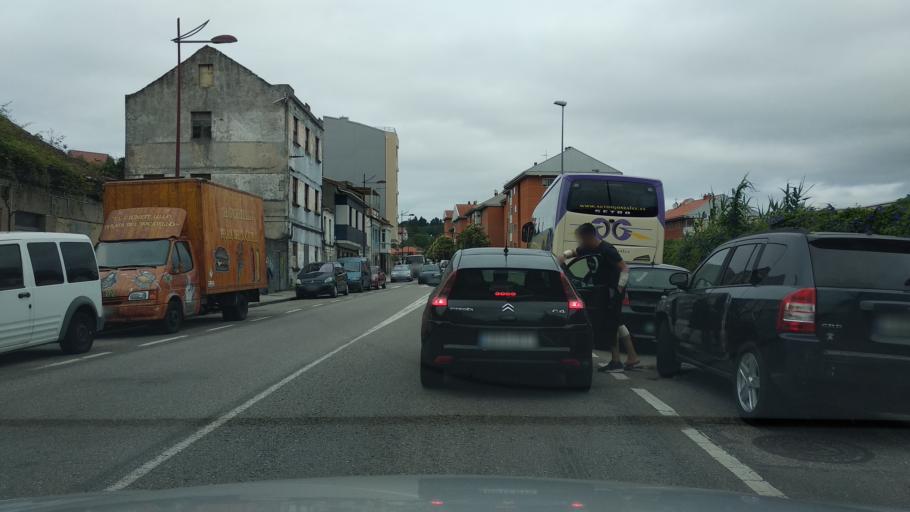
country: ES
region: Galicia
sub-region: Provincia de Pontevedra
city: Vigo
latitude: 42.2508
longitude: -8.6904
